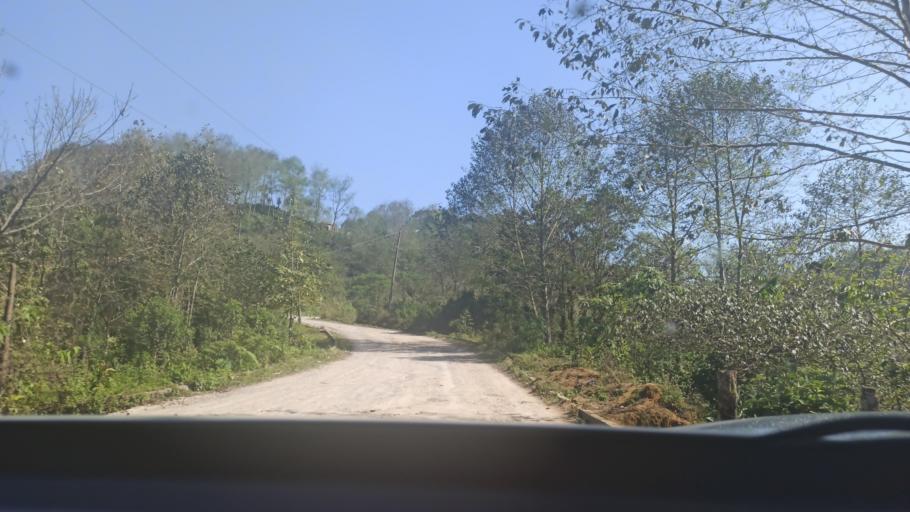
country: MX
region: Veracruz
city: Xocotla
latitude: 18.9726
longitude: -97.0907
